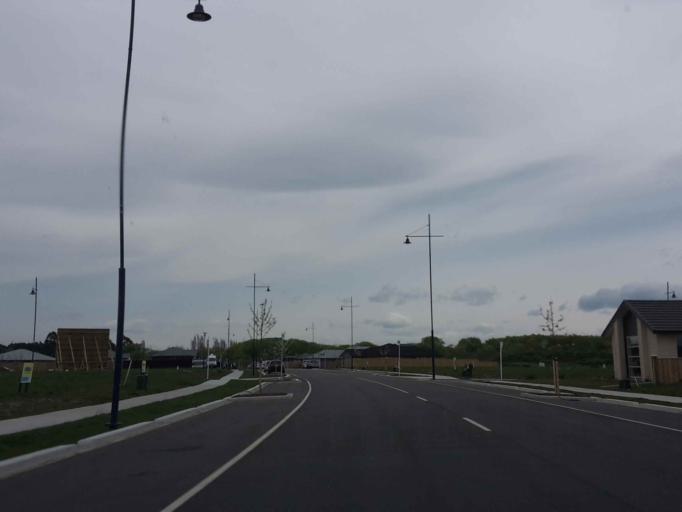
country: NZ
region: Canterbury
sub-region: Waimakariri District
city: Woodend
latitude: -43.3044
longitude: 172.6973
